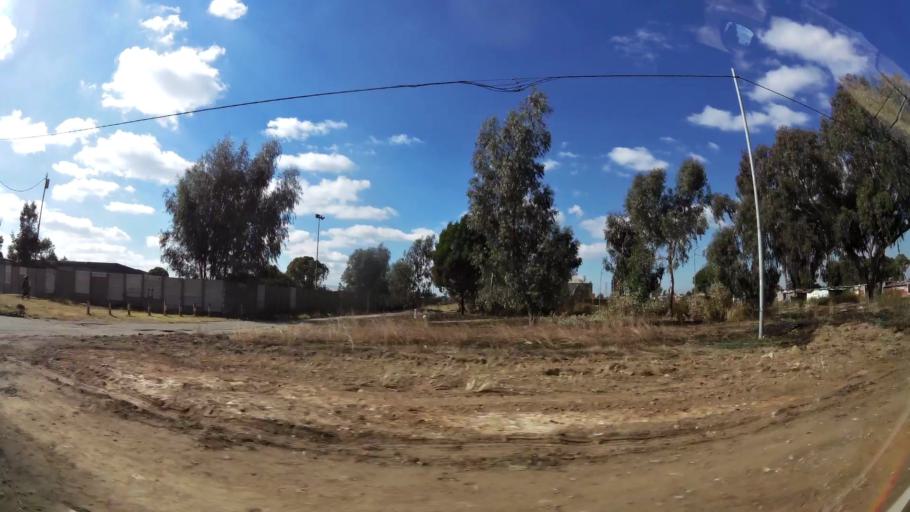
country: ZA
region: Gauteng
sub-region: West Rand District Municipality
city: Krugersdorp
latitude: -26.1299
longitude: 27.8017
